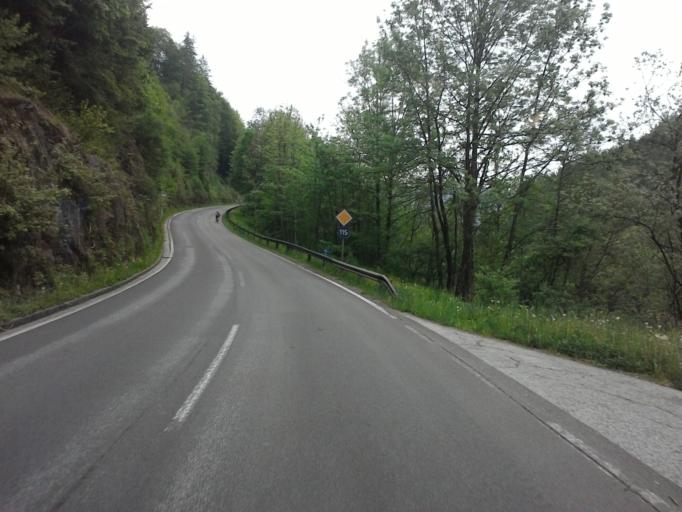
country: AT
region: Styria
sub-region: Politischer Bezirk Liezen
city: Gams bei Hieflau
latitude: 47.6356
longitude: 14.7598
